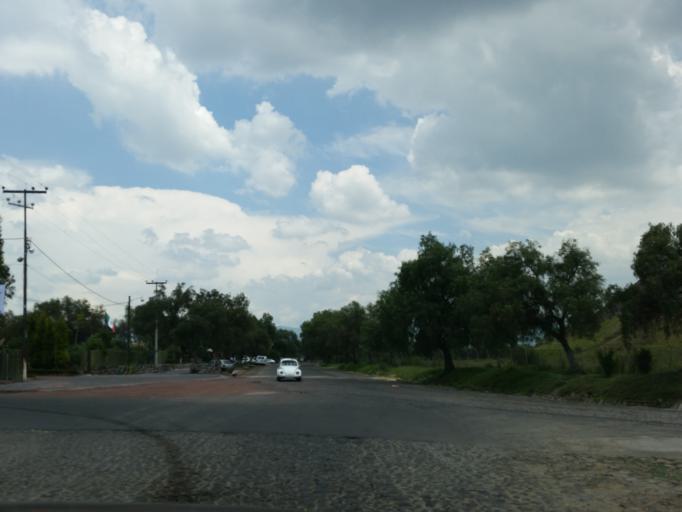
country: MX
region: Morelos
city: San Martin de las Piramides
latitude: 19.7011
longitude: -98.8449
